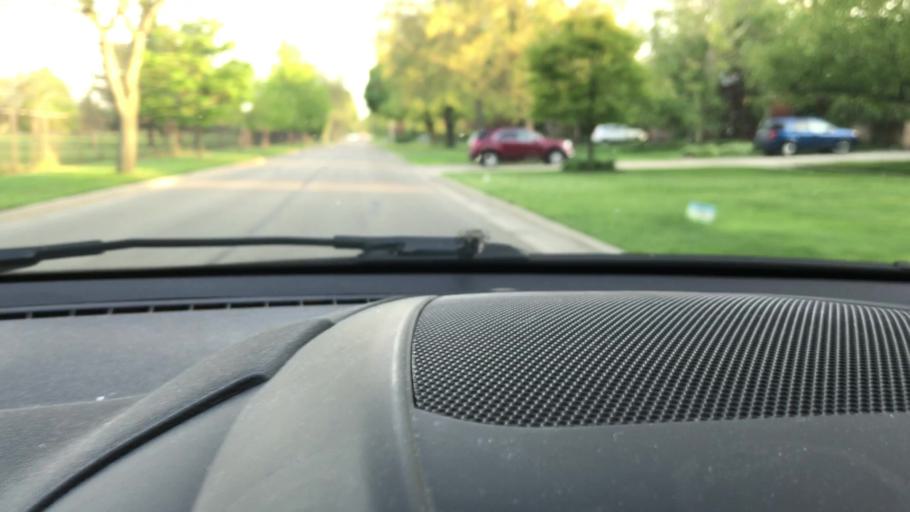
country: US
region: Michigan
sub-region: Oakland County
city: Huntington Woods
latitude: 42.4799
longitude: -83.1731
